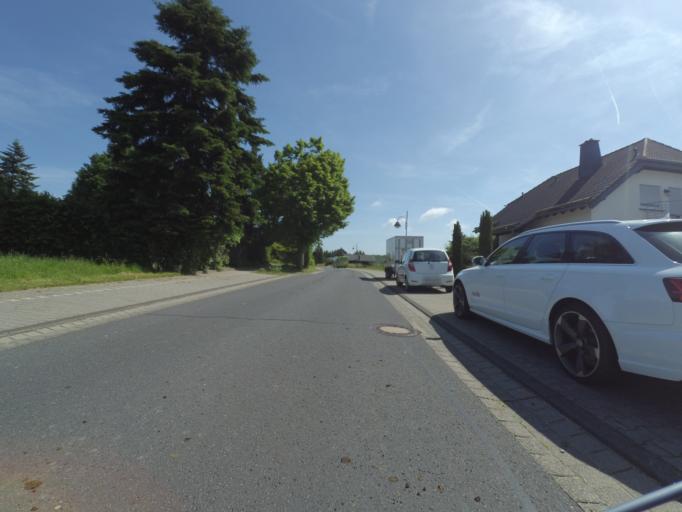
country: DE
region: Rheinland-Pfalz
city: Eppenberg
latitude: 50.2506
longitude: 7.0717
